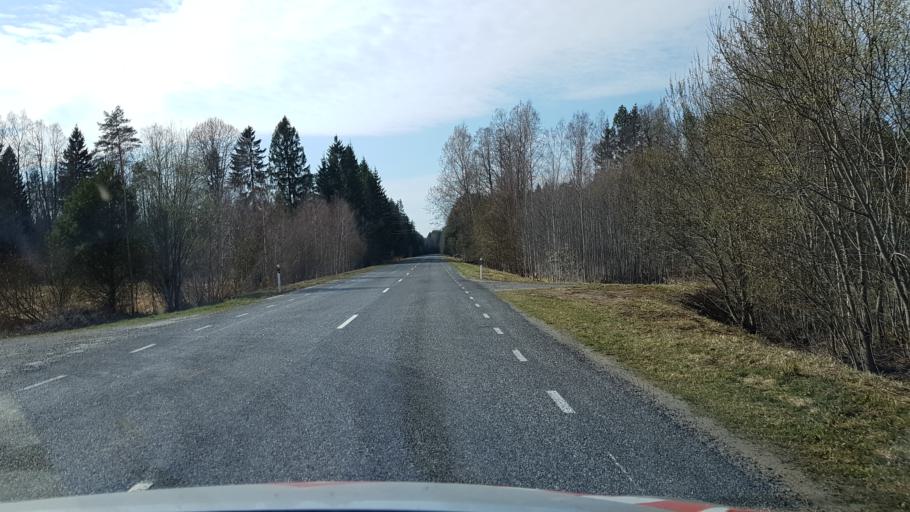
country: EE
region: Harju
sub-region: Loksa linn
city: Loksa
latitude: 59.5629
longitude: 25.9589
